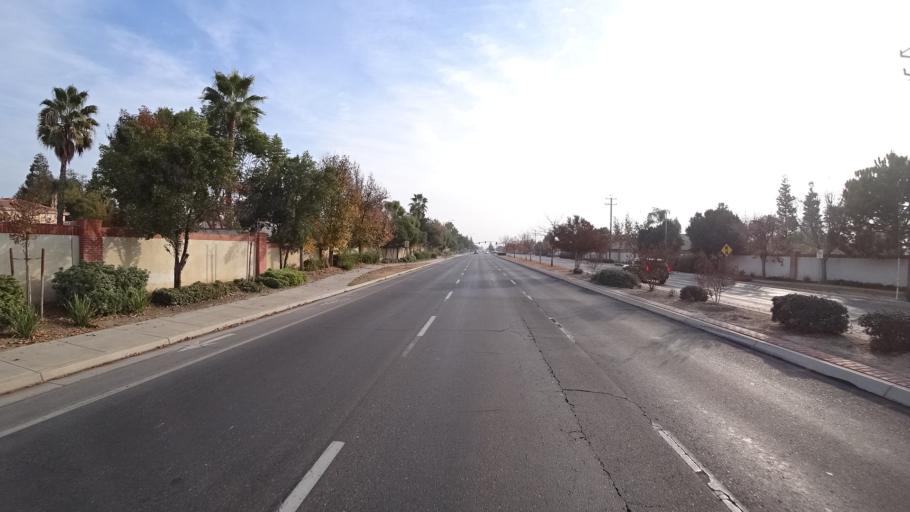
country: US
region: California
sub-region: Kern County
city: Greenacres
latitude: 35.3330
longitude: -119.1279
